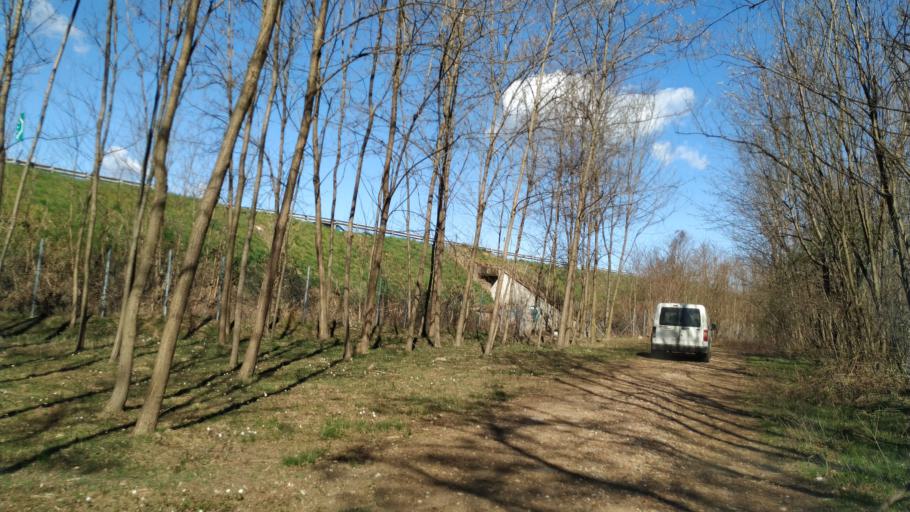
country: IT
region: Piedmont
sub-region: Provincia di Novara
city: Ghemme
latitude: 45.6008
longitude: 8.4032
